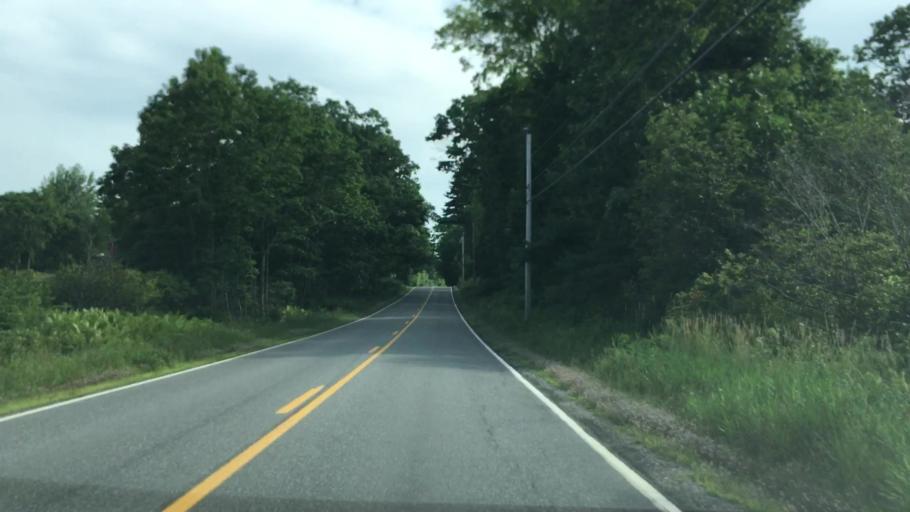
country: US
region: Maine
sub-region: Waldo County
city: Belfast
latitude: 44.3934
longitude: -69.0328
